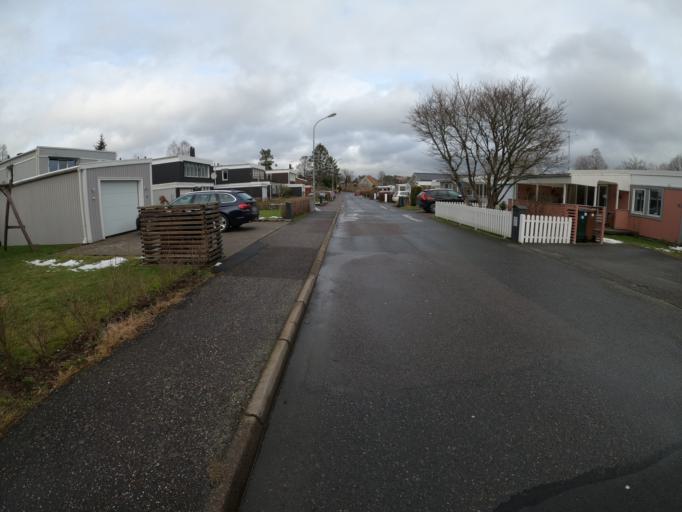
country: SE
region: Vaestra Goetaland
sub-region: Harryda Kommun
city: Molnlycke
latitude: 57.6471
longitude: 12.1186
